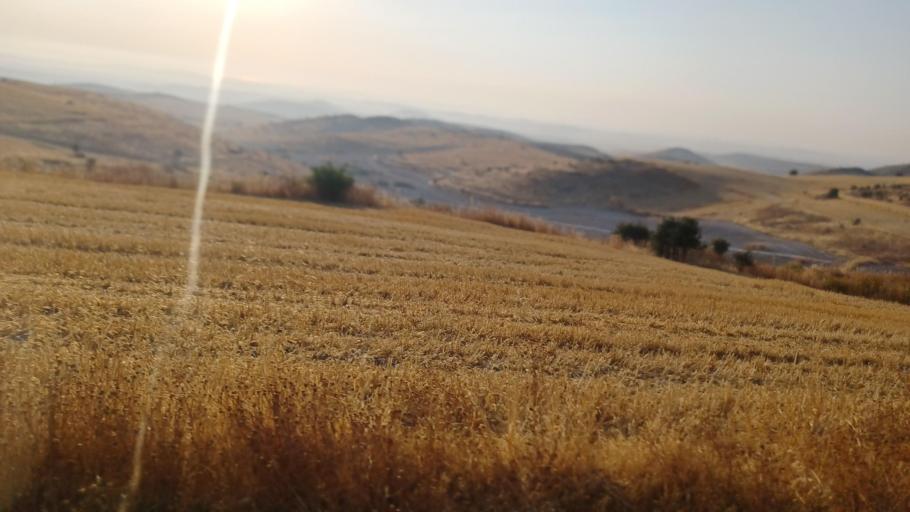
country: CY
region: Larnaka
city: Psevdas
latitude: 34.9083
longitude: 33.4922
